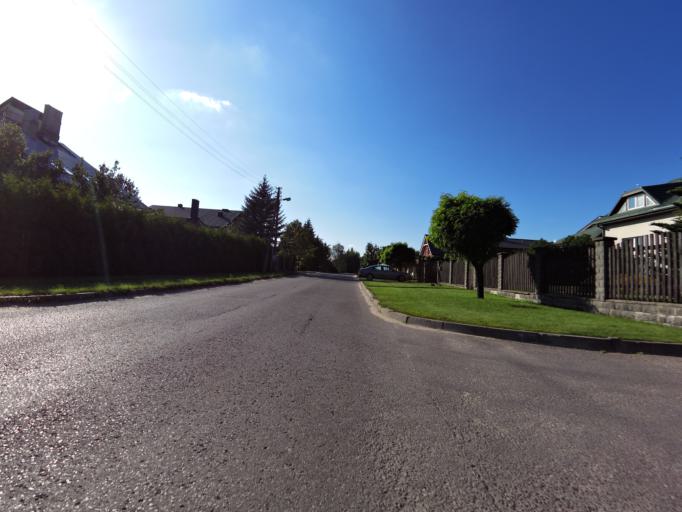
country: LT
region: Vilnius County
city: Pasilaiciai
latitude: 54.7294
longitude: 25.1930
